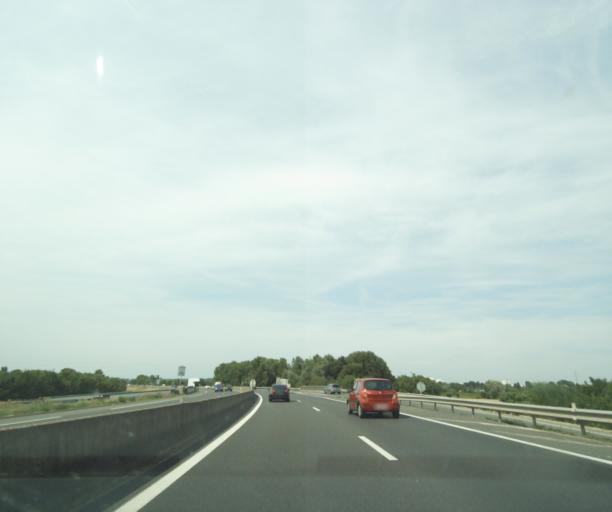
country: FR
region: Centre
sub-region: Departement d'Indre-et-Loire
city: Joue-les-Tours
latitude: 47.3683
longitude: 0.6552
